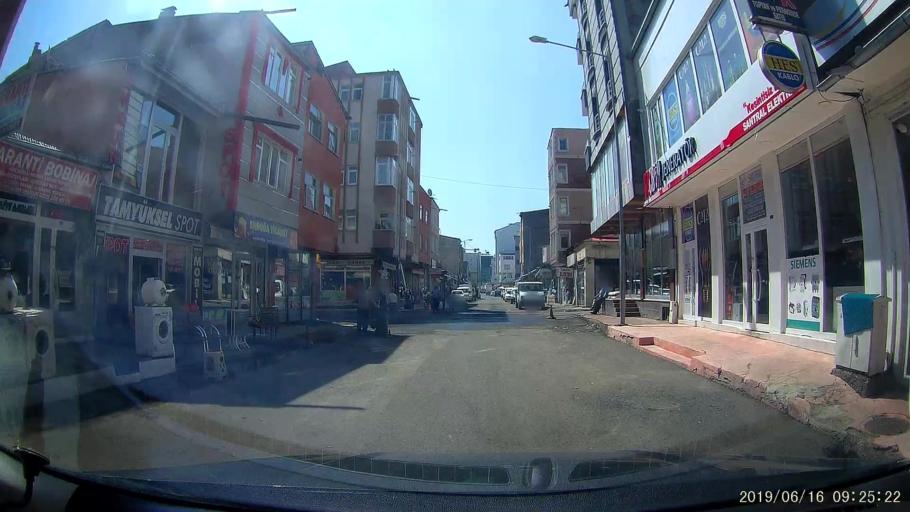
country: TR
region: Kars
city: Kars
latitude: 40.6091
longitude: 43.0955
